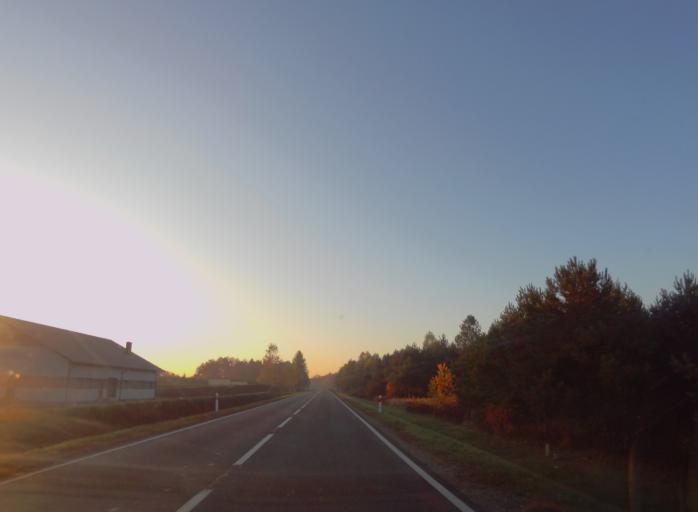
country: PL
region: Subcarpathian Voivodeship
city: Nowa Sarzyna
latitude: 50.3390
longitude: 22.3300
